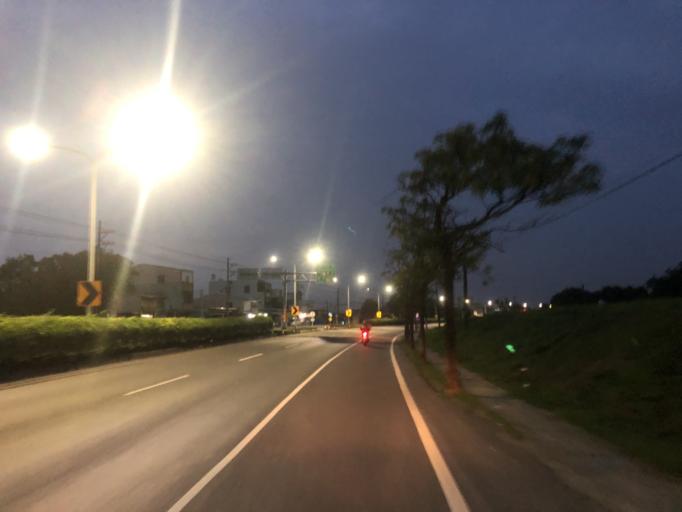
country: TW
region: Taiwan
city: Yujing
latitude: 23.1700
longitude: 120.3388
